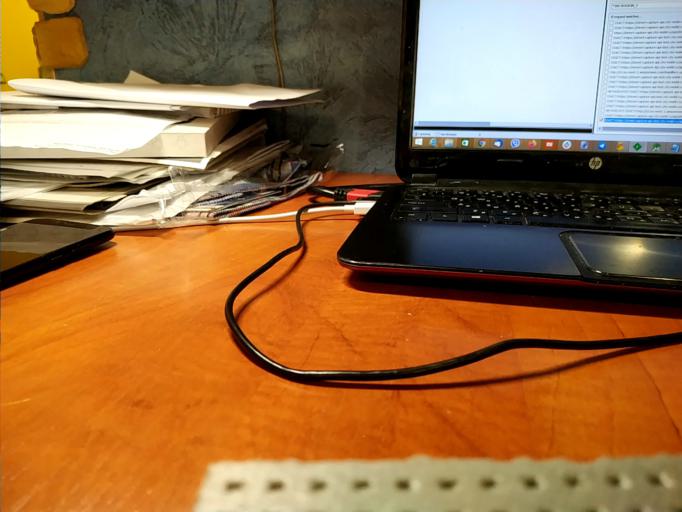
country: RU
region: Tverskaya
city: Spirovo
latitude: 57.4512
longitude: 34.9200
